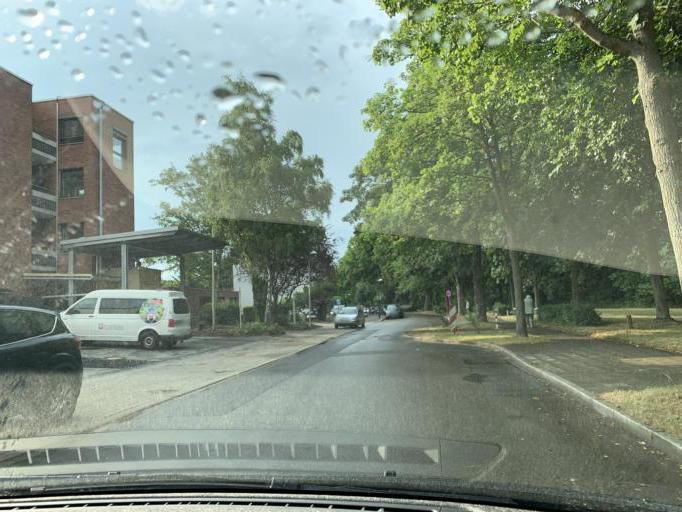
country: DE
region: North Rhine-Westphalia
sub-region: Regierungsbezirk Koln
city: Dueren
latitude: 50.7924
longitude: 6.4774
